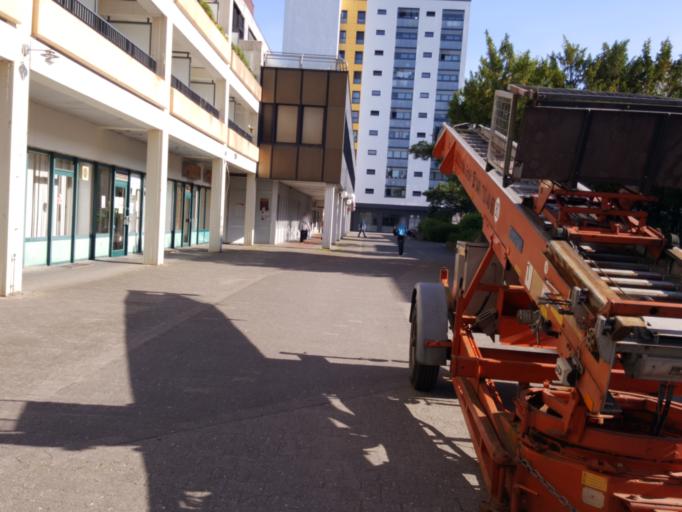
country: DE
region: Schleswig-Holstein
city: Oststeinbek
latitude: 53.5284
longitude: 10.1482
